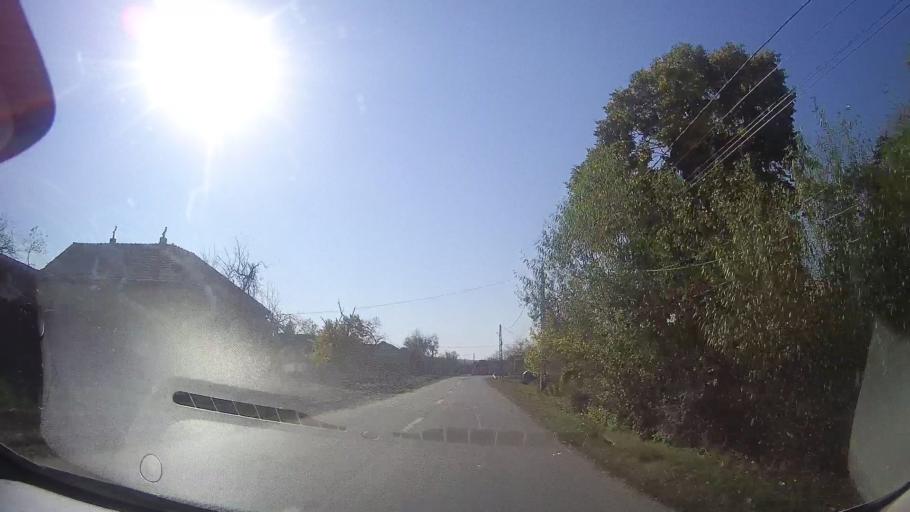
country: RO
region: Timis
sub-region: Comuna Secas
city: Secas
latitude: 45.8461
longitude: 21.7931
